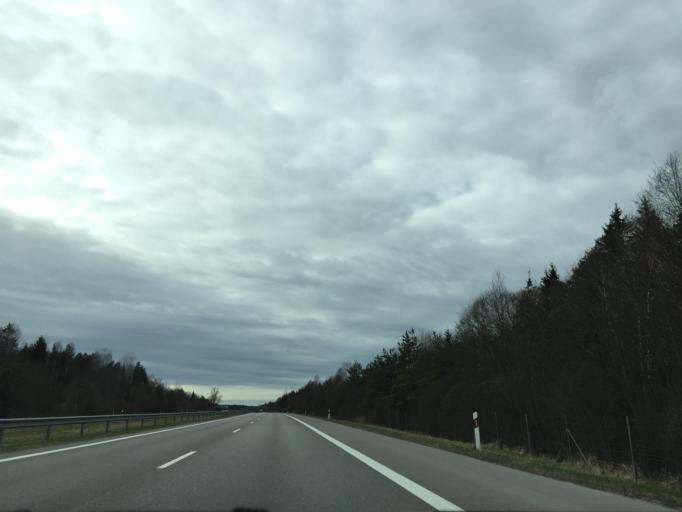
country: LT
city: Silale
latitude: 55.6090
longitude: 22.0704
